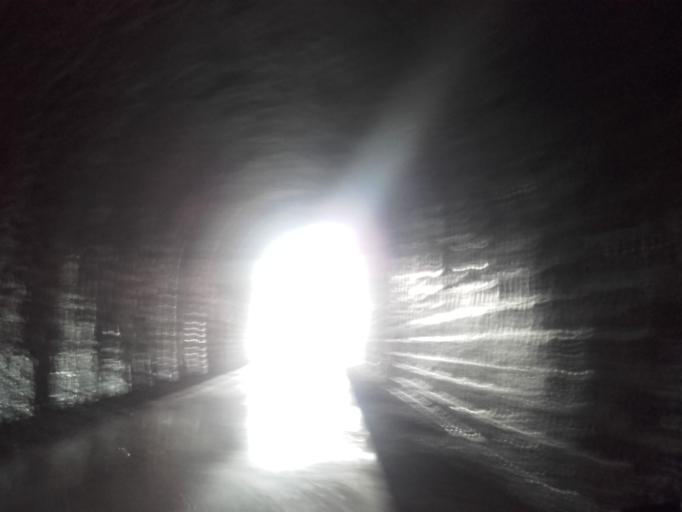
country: FR
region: Bourgogne
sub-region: Departement de la Cote-d'Or
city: Nolay
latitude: 46.9080
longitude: 4.6513
